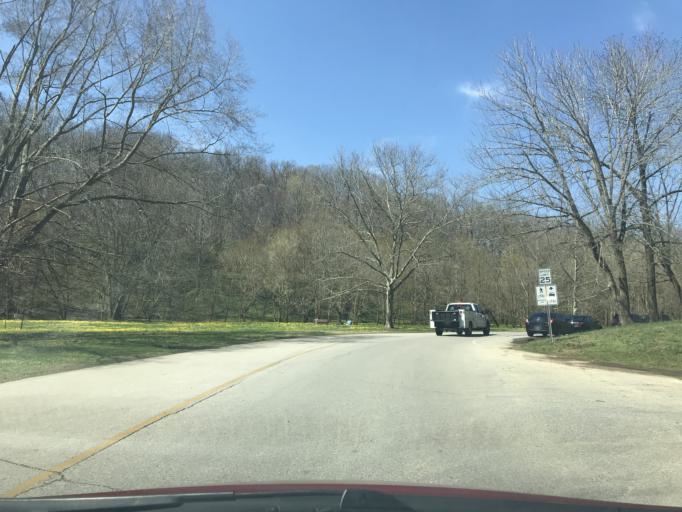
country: US
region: Kentucky
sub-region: Jefferson County
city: Saint Matthews
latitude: 38.2394
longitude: -85.6940
